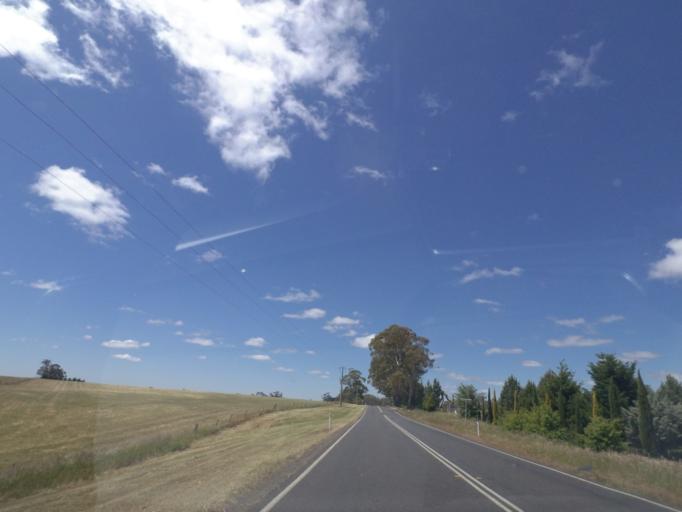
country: AU
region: Victoria
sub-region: Mount Alexander
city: Castlemaine
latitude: -37.3292
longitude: 144.1879
